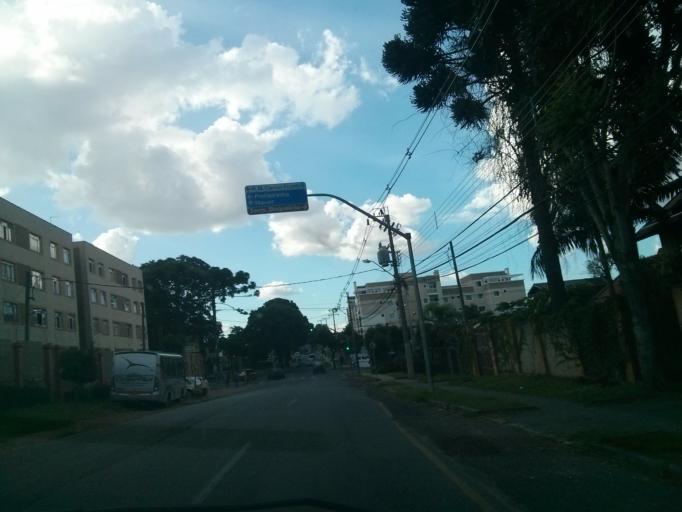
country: BR
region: Parana
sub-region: Sao Jose Dos Pinhais
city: Sao Jose dos Pinhais
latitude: -25.5227
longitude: -49.2397
